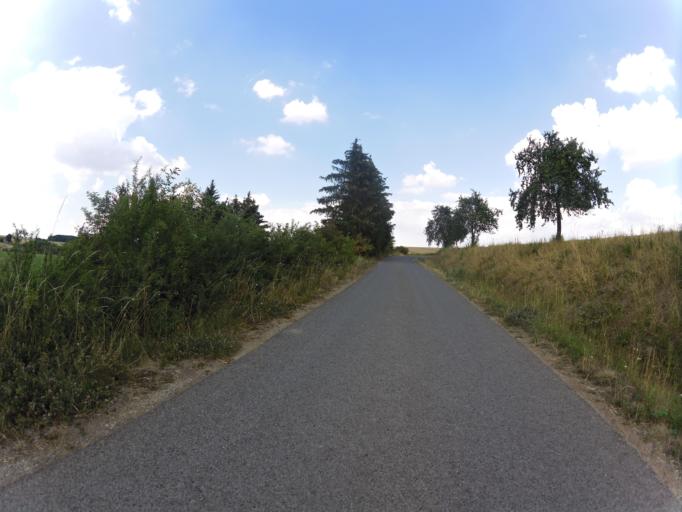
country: DE
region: Bavaria
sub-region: Regierungsbezirk Unterfranken
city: Ochsenfurt
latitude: 49.6488
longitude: 10.0613
